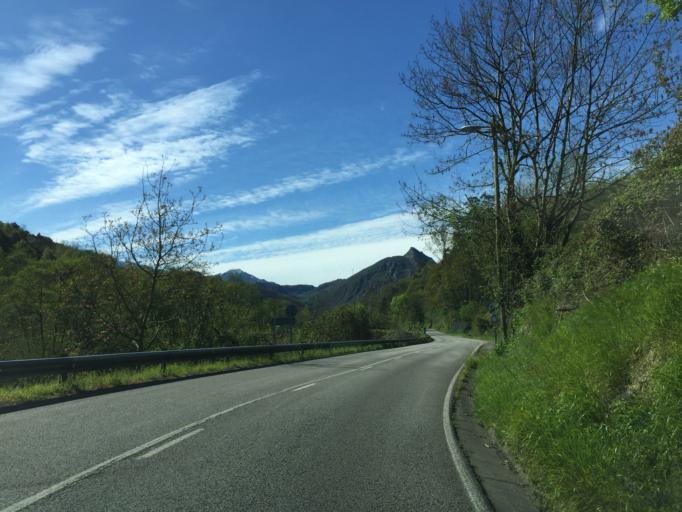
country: ES
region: Asturias
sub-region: Province of Asturias
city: Proaza
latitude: 43.3354
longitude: -5.9865
